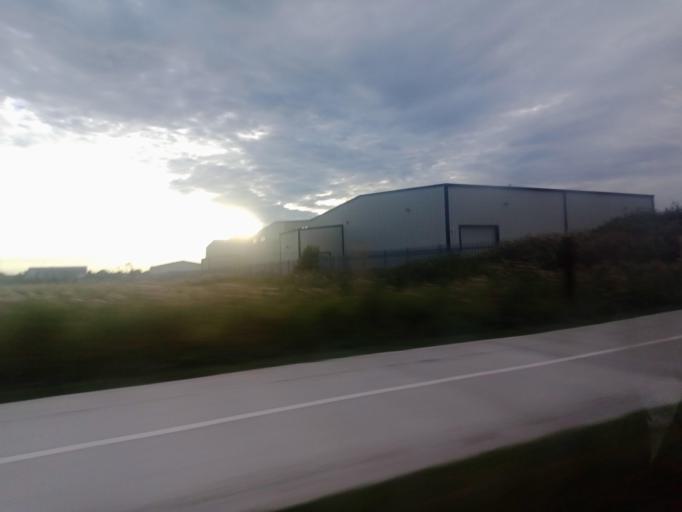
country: IE
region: Leinster
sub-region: Laois
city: Portlaoise
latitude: 53.0241
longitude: -7.3162
